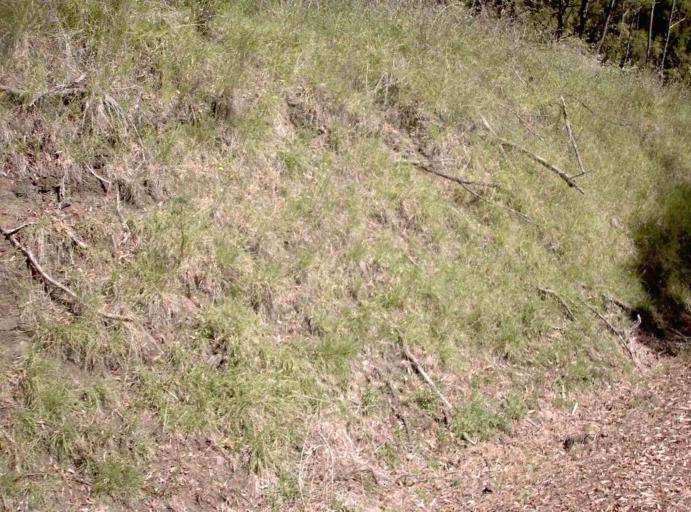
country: AU
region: Victoria
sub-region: East Gippsland
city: Lakes Entrance
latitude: -37.3503
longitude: 148.2287
